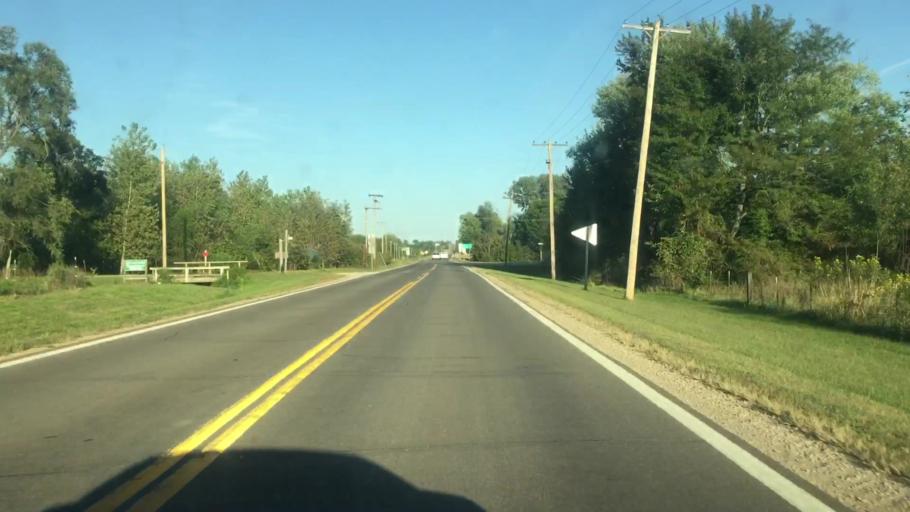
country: US
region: Kansas
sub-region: Brown County
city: Horton
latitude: 39.5505
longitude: -95.5170
